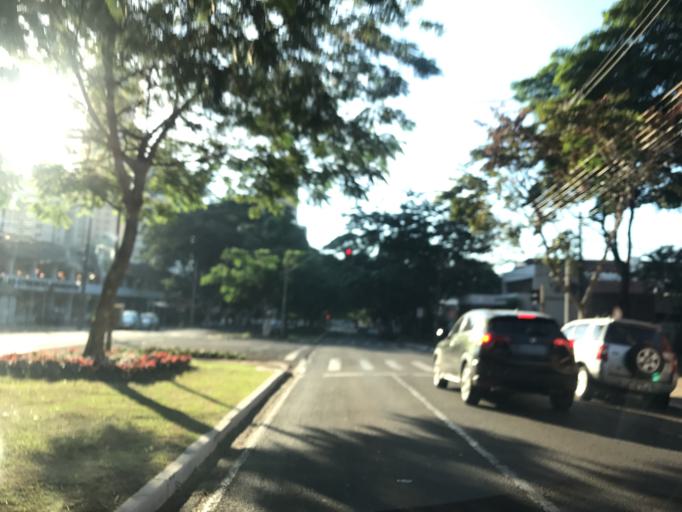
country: BR
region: Parana
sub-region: Maringa
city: Maringa
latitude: -23.4256
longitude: -51.9471
